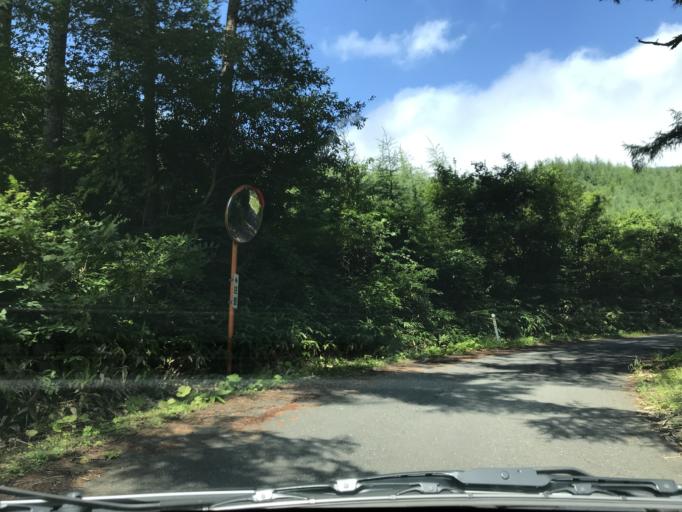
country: JP
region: Iwate
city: Ofunato
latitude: 38.9867
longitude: 141.4329
